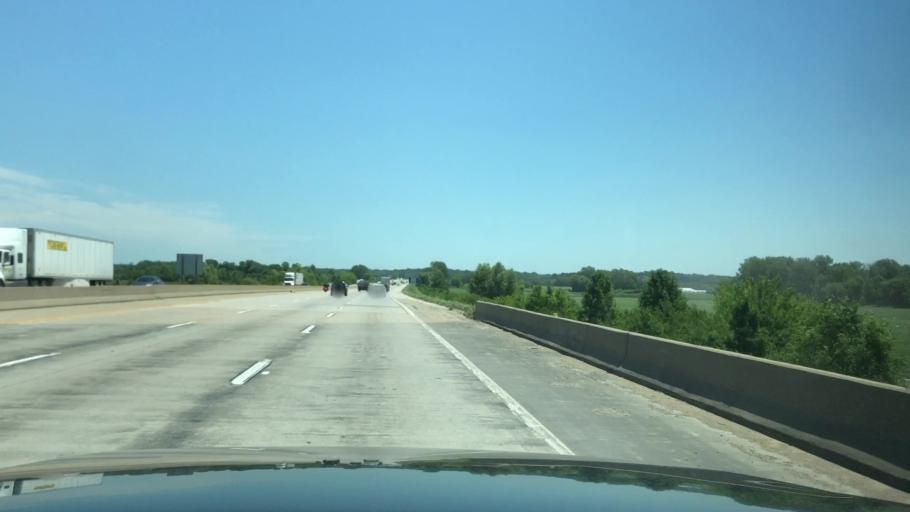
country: US
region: Missouri
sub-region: Saint Charles County
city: Saint Charles
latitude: 38.7915
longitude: -90.4436
